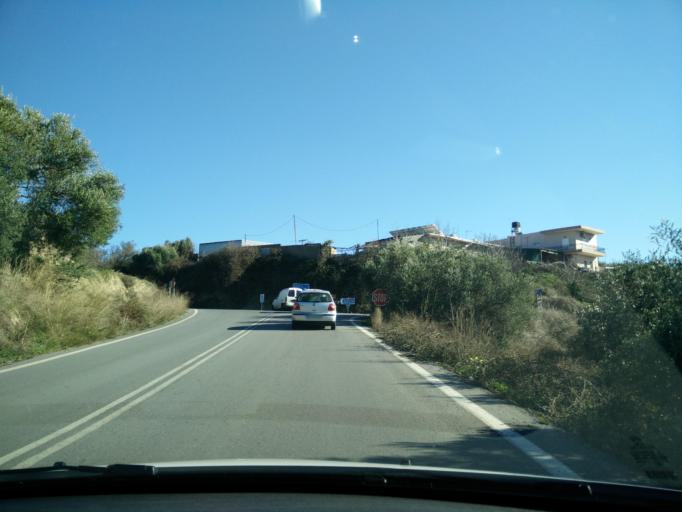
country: GR
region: Crete
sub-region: Nomos Irakleiou
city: Arkalochori
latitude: 35.1378
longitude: 25.2610
